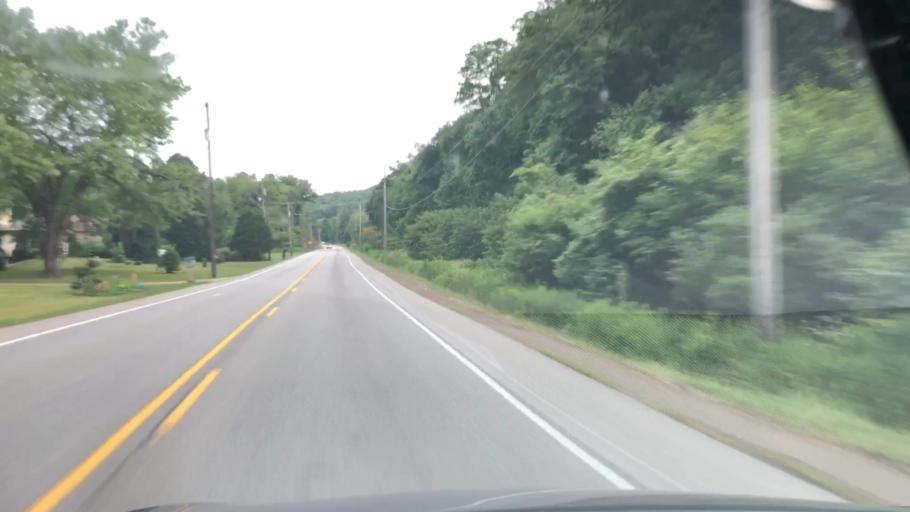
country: US
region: Pennsylvania
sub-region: Venango County
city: Hasson Heights
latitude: 41.5101
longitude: -79.7026
